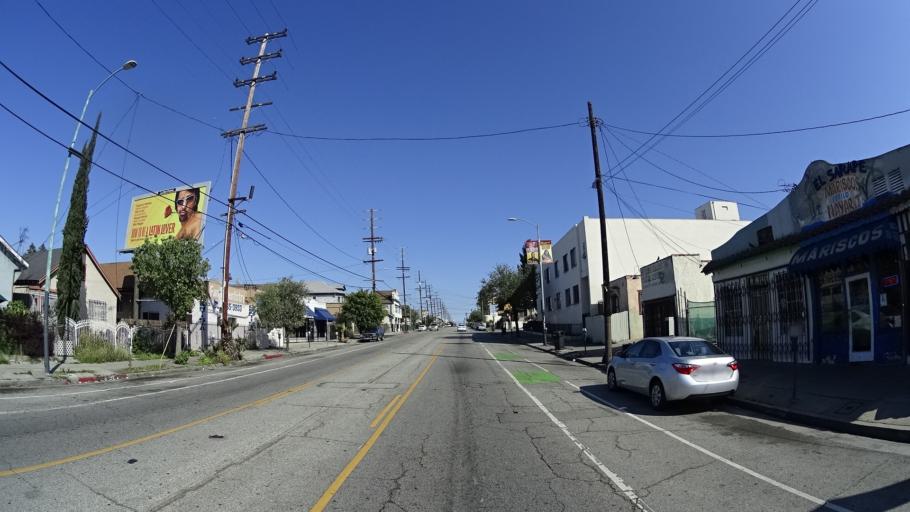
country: US
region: California
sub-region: Los Angeles County
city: Boyle Heights
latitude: 34.0429
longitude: -118.2081
